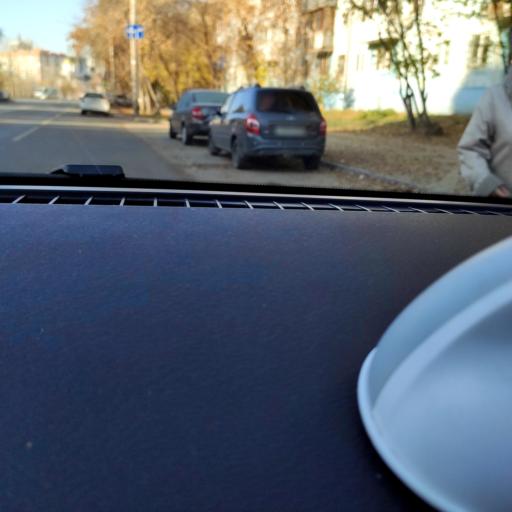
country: RU
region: Samara
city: Samara
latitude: 53.1963
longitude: 50.1611
